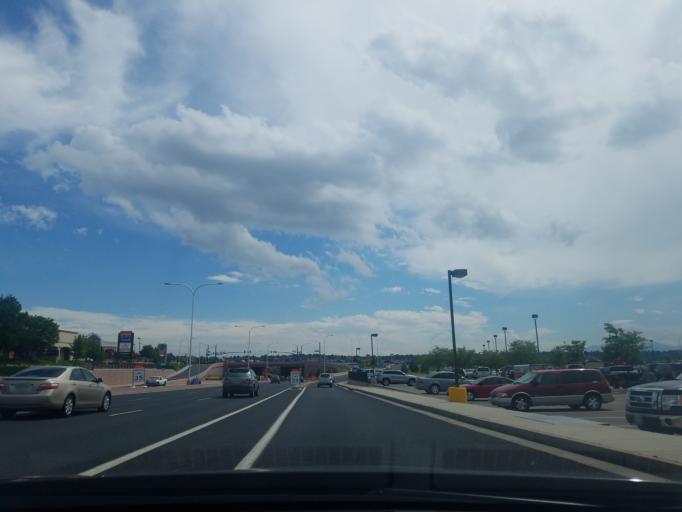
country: US
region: Colorado
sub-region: El Paso County
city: Air Force Academy
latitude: 38.9354
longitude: -104.7976
